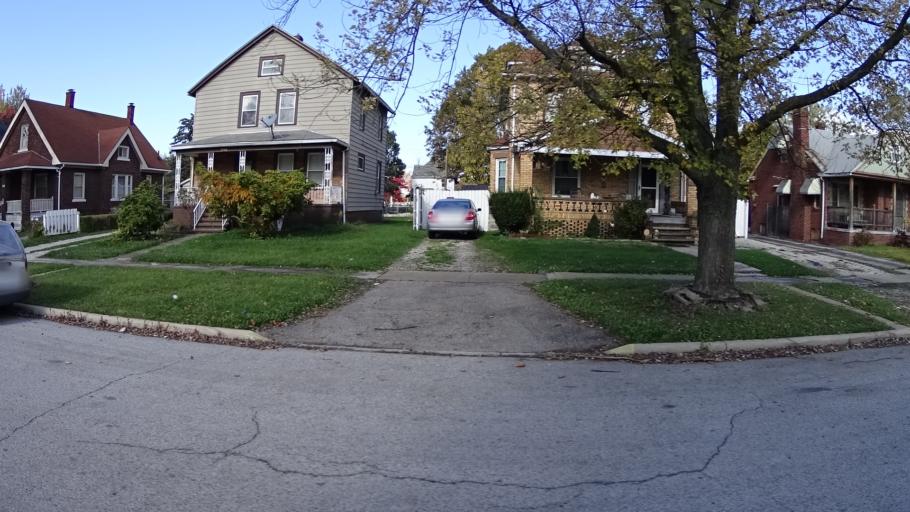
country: US
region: Ohio
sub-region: Lorain County
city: Lorain
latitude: 41.4410
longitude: -82.1390
